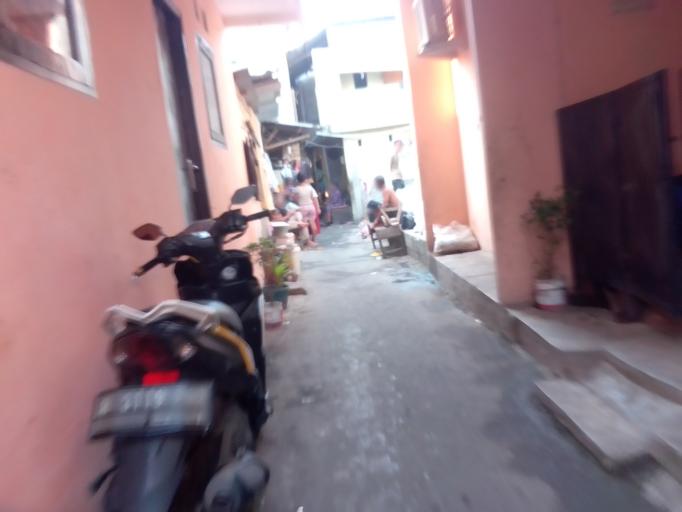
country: ID
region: Jakarta Raya
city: Jakarta
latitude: -6.1931
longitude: 106.8108
